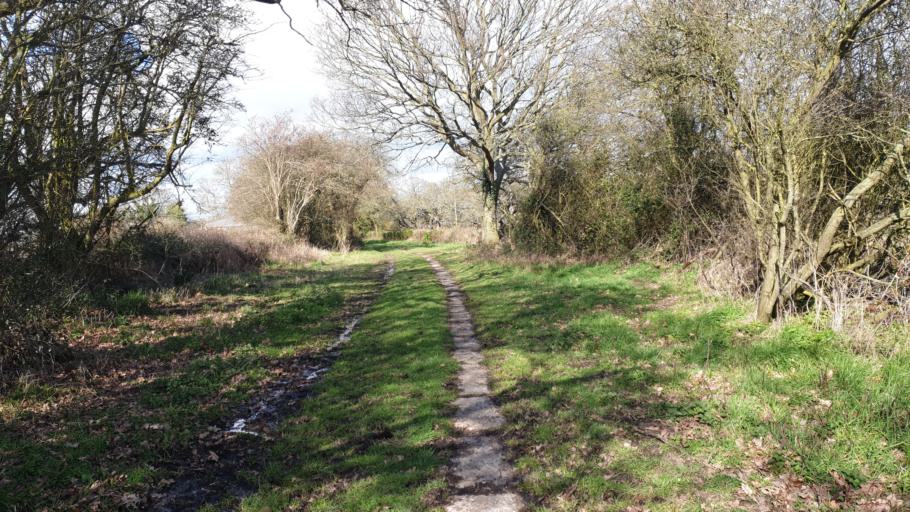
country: GB
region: England
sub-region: Essex
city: Little Clacton
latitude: 51.8440
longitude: 1.1629
